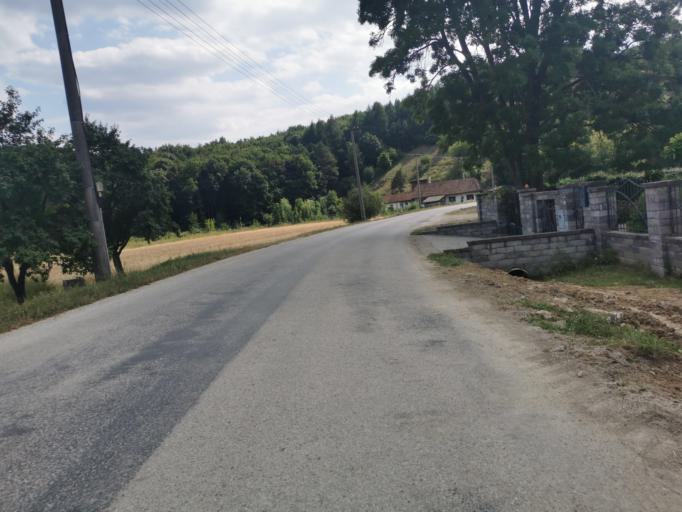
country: SK
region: Trenciansky
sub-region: Okres Myjava
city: Myjava
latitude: 48.7482
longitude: 17.5258
